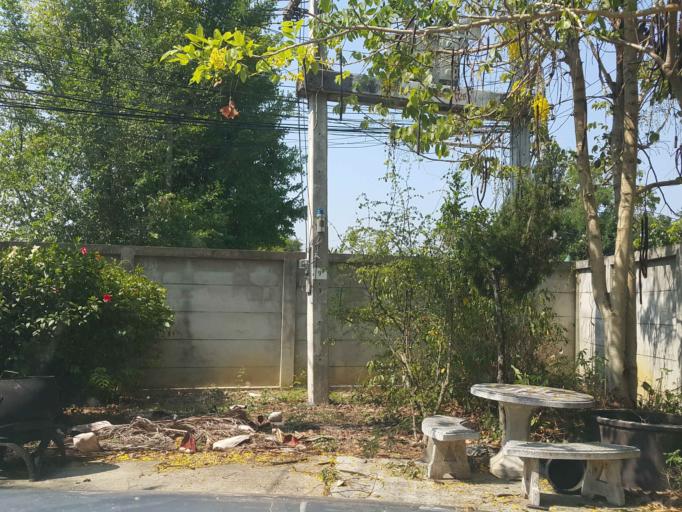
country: TH
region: Chiang Mai
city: Saraphi
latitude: 18.7616
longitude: 99.0528
